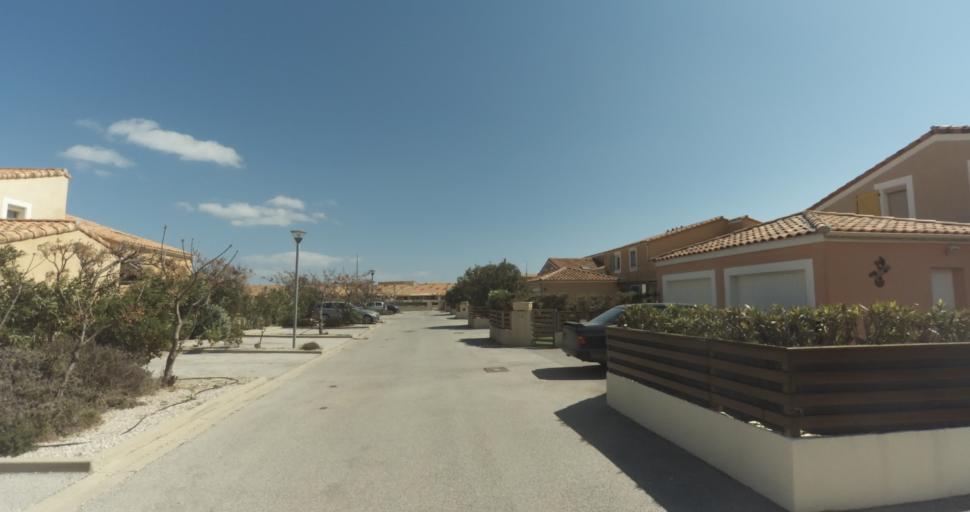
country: FR
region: Languedoc-Roussillon
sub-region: Departement de l'Aude
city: Leucate
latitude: 42.8679
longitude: 3.0435
